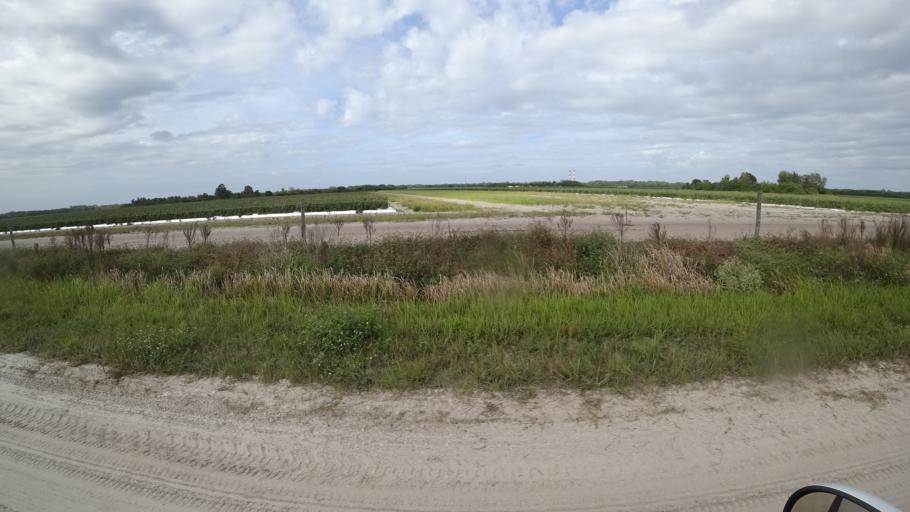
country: US
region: Florida
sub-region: Hillsborough County
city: Wimauma
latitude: 27.5882
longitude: -82.3124
